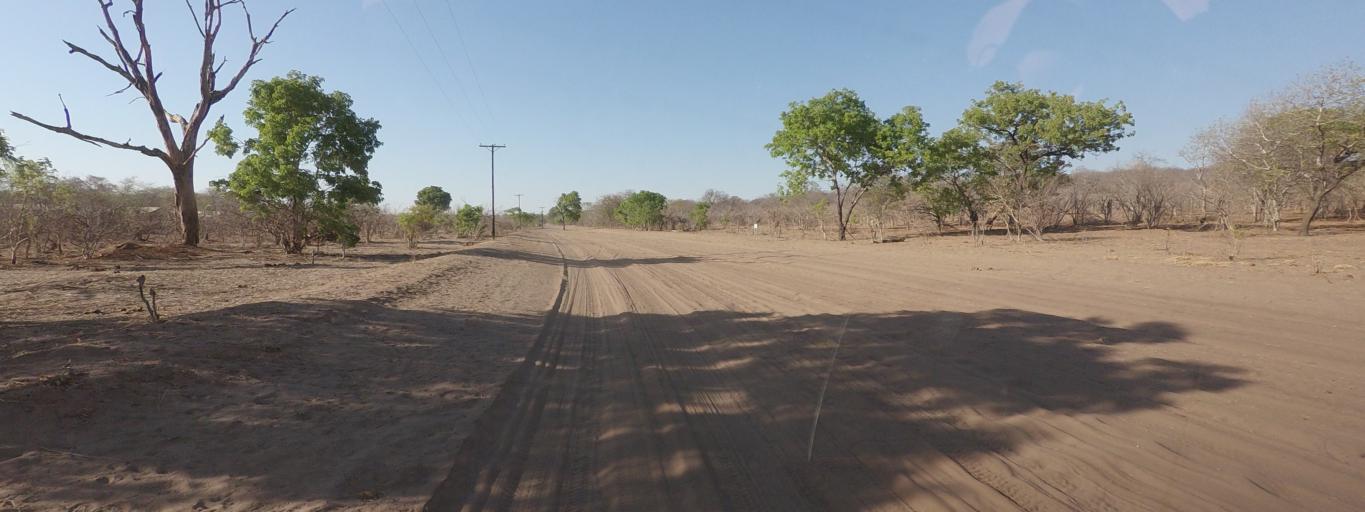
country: BW
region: North West
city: Kasane
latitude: -17.8871
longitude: 25.2298
